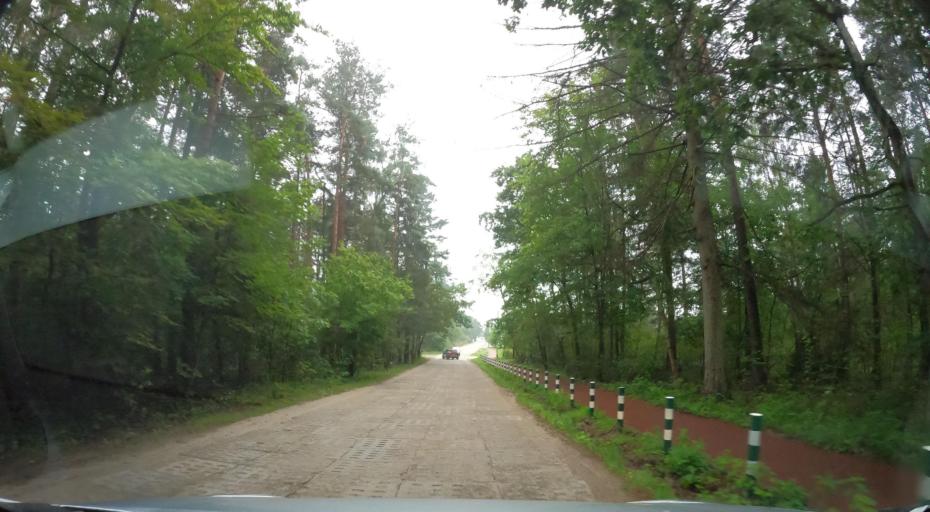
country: PL
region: Pomeranian Voivodeship
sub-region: Powiat kartuski
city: Chwaszczyno
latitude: 54.4331
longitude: 18.4177
